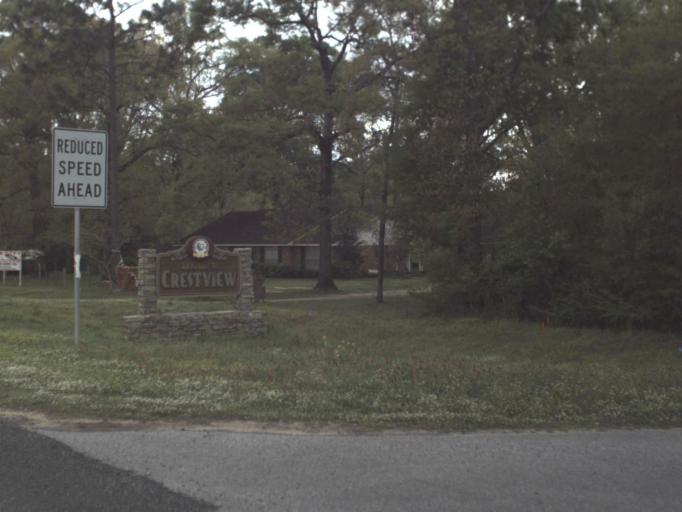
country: US
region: Florida
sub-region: Okaloosa County
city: Crestview
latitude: 30.7972
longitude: -86.5567
